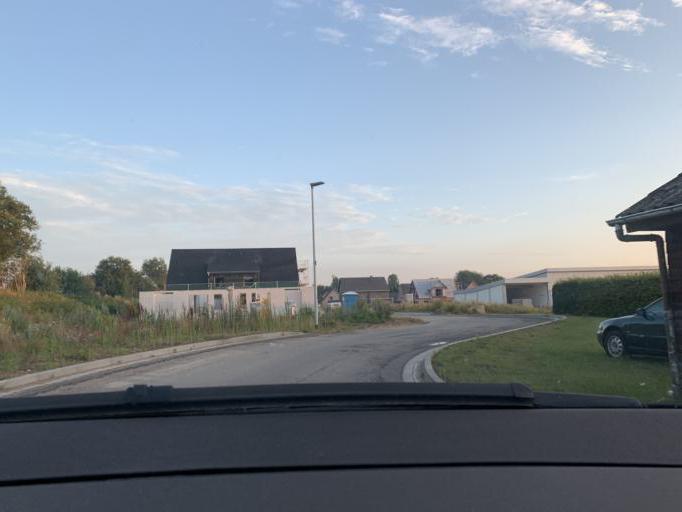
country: DE
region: Schleswig-Holstein
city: Mildstedt
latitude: 54.4705
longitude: 9.0935
